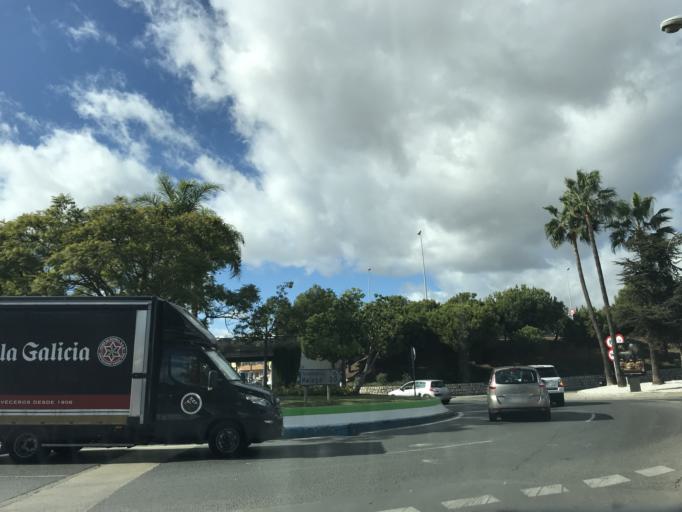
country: ES
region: Andalusia
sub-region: Provincia de Malaga
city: Fuengirola
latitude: 36.5396
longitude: -4.6342
